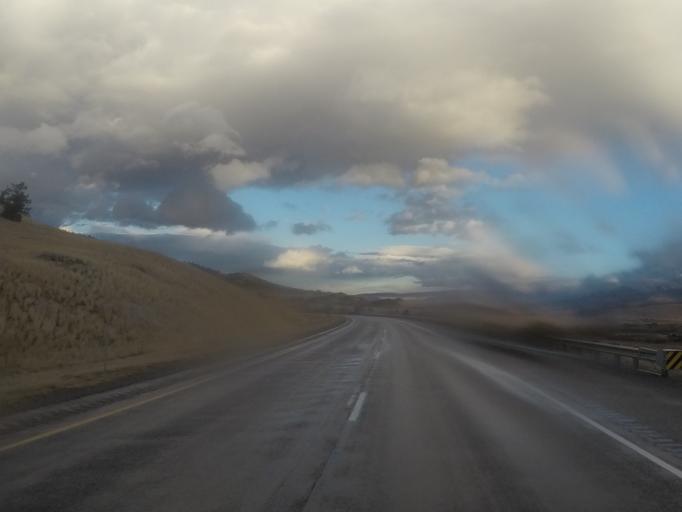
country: US
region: Montana
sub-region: Park County
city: Livingston
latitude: 45.6599
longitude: -110.6562
